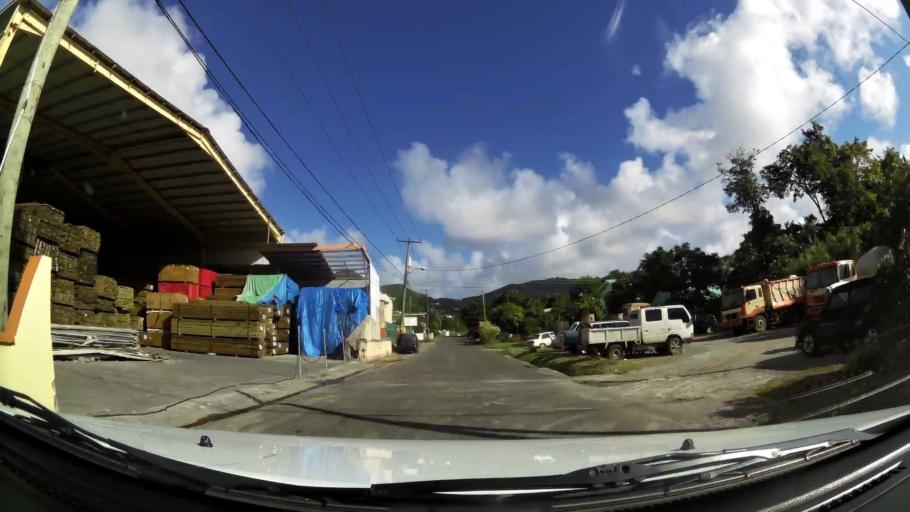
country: LC
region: Castries Quarter
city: Bisee
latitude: 14.0436
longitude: -60.9604
